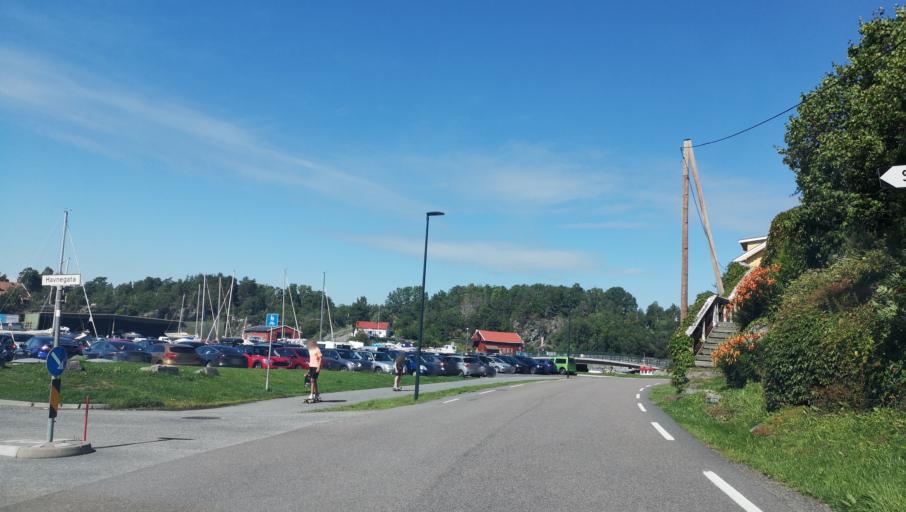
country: NO
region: Ostfold
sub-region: Moss
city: Moss
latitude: 59.5265
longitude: 10.6897
